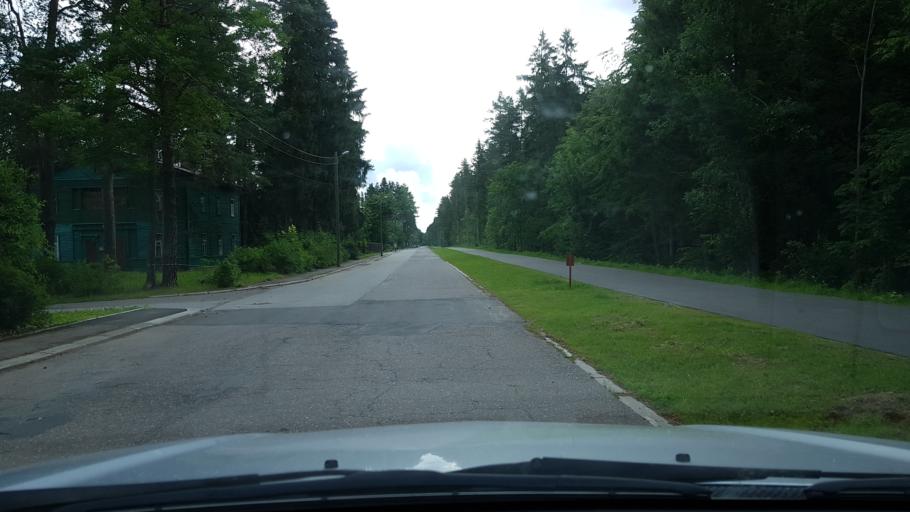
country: EE
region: Ida-Virumaa
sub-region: Narva-Joesuu linn
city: Narva-Joesuu
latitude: 59.4465
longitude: 28.0263
